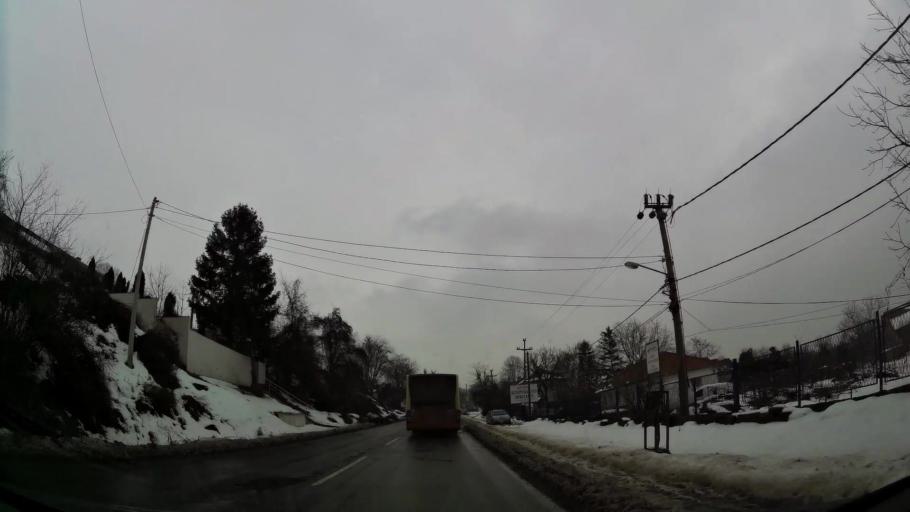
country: RS
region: Central Serbia
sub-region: Belgrade
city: Zvezdara
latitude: 44.7769
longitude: 20.5322
